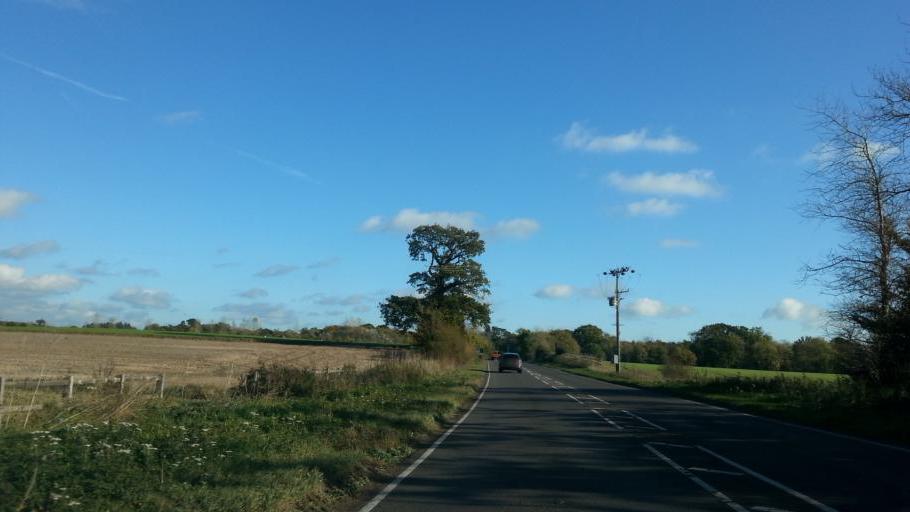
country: GB
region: England
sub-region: Suffolk
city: Beccles
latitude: 52.4759
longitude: 1.5398
